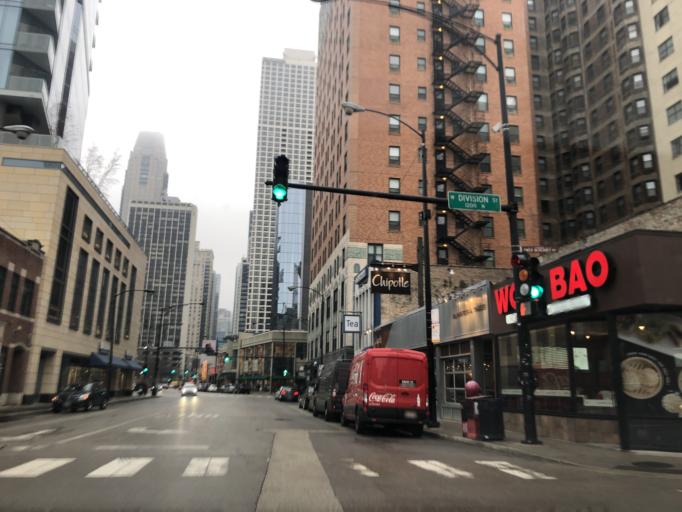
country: US
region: Illinois
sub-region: Cook County
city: Chicago
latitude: 41.9040
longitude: -87.6287
